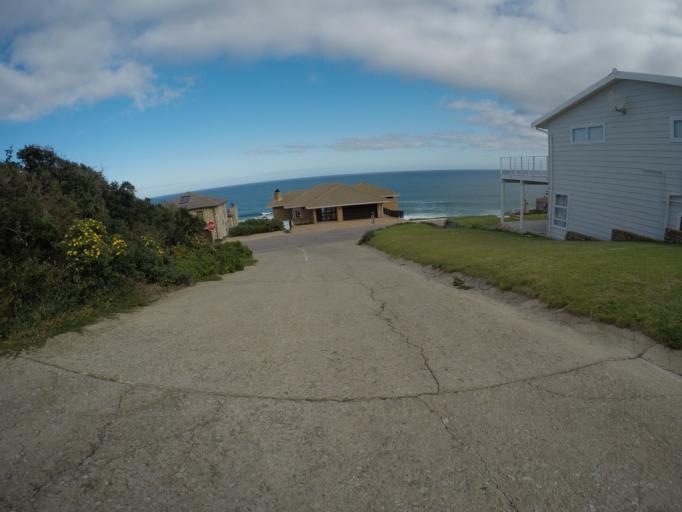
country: ZA
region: Western Cape
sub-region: Eden District Municipality
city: Riversdale
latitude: -34.4310
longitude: 21.3311
